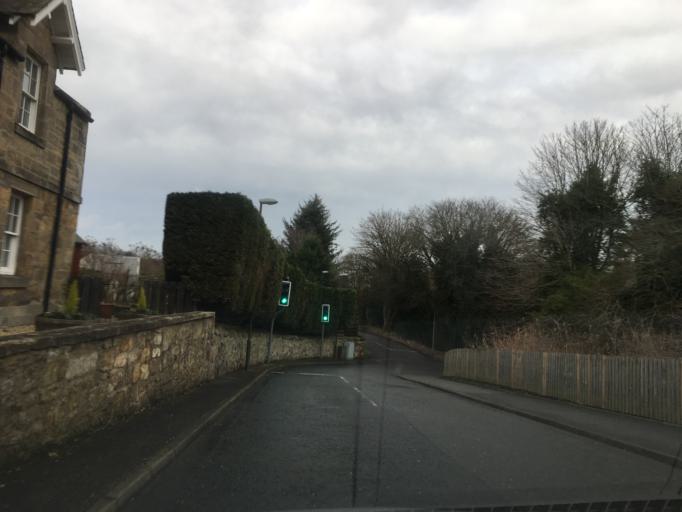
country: GB
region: Scotland
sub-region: Midlothian
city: Penicuik
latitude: 55.8317
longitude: -3.2084
